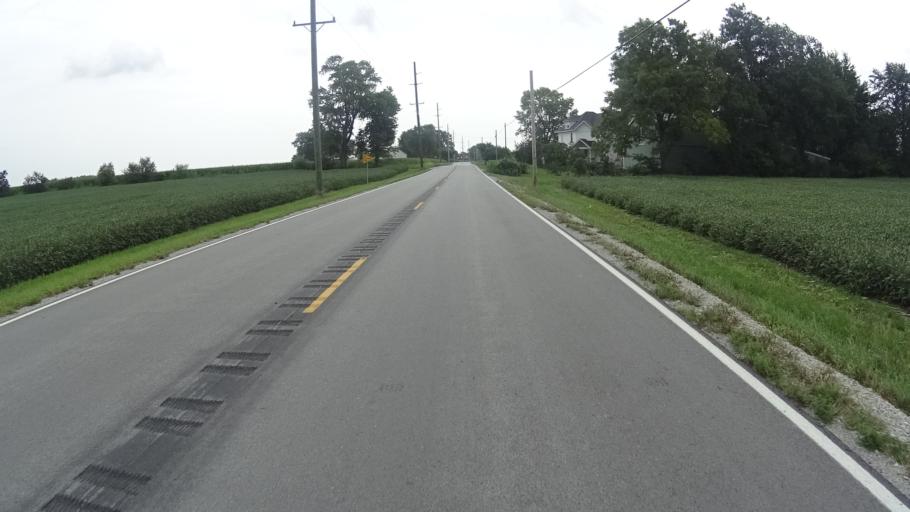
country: US
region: Indiana
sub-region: Madison County
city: Lapel
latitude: 40.0173
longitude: -85.8305
